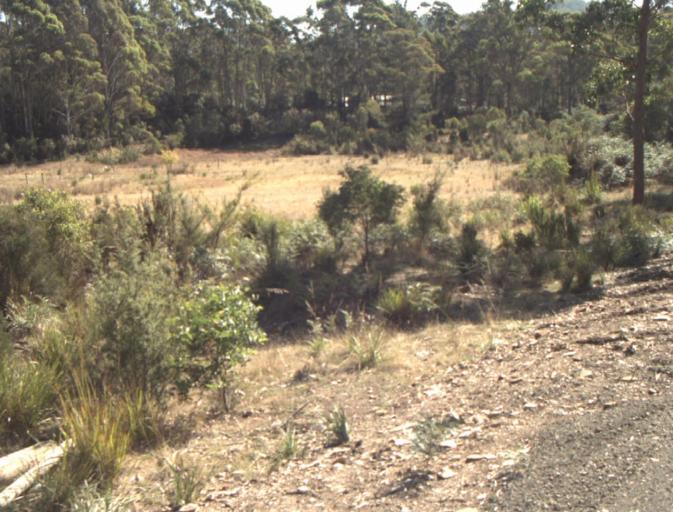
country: AU
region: Tasmania
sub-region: Launceston
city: Mayfield
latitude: -41.2757
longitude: 147.1084
